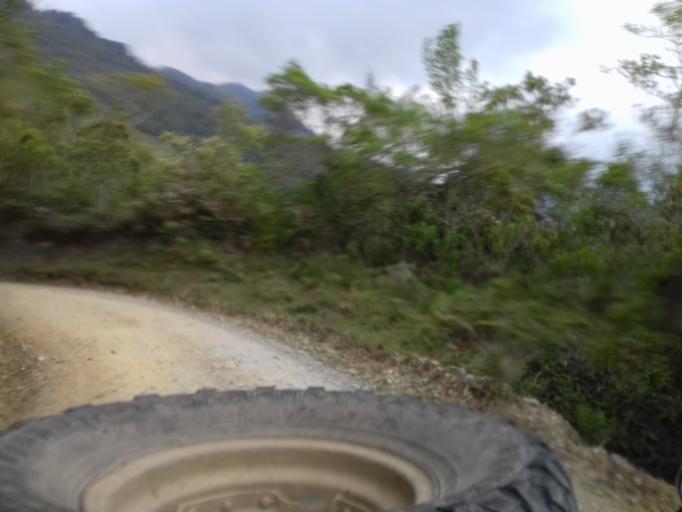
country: CO
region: Quindio
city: Salento
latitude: 4.6096
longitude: -75.5473
